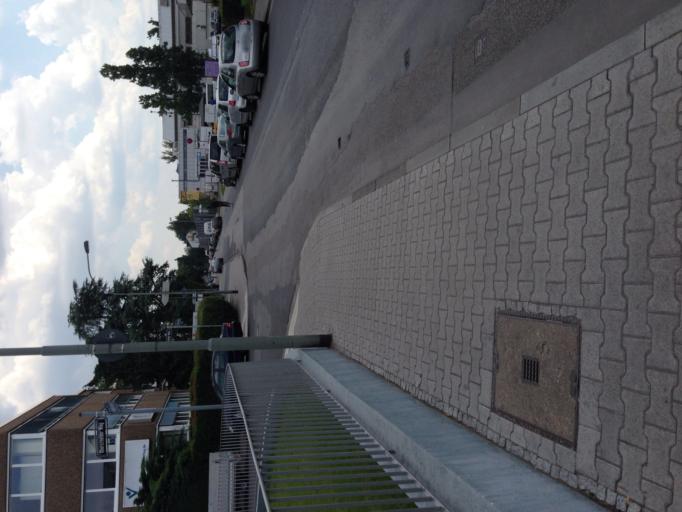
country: DE
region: Hesse
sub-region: Regierungsbezirk Darmstadt
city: Steinbach am Taunus
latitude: 50.1634
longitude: 8.6362
